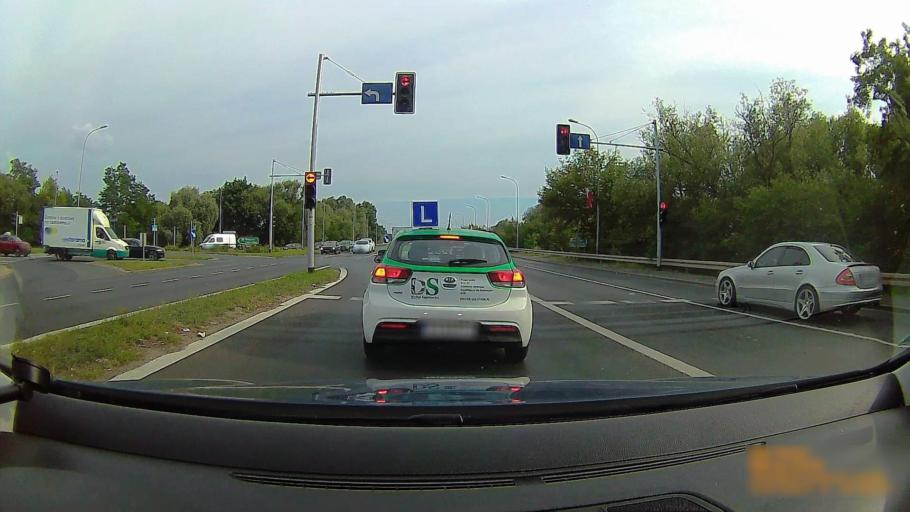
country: PL
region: Greater Poland Voivodeship
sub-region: Konin
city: Konin
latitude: 52.2234
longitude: 18.2502
